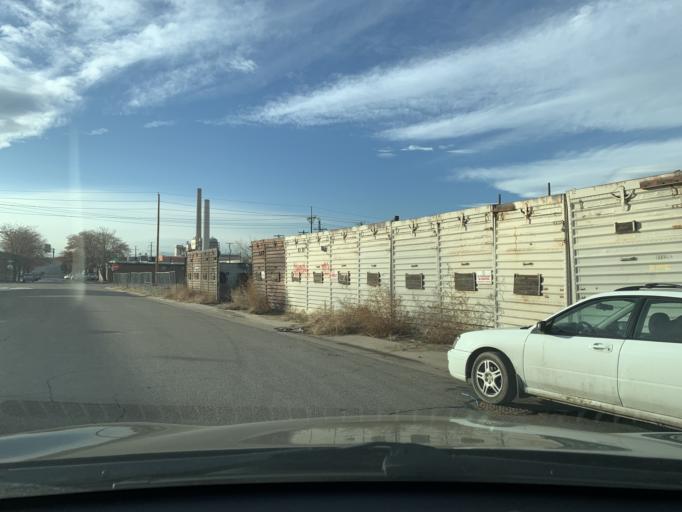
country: US
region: Colorado
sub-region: Denver County
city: Denver
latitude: 39.7361
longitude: -105.0113
